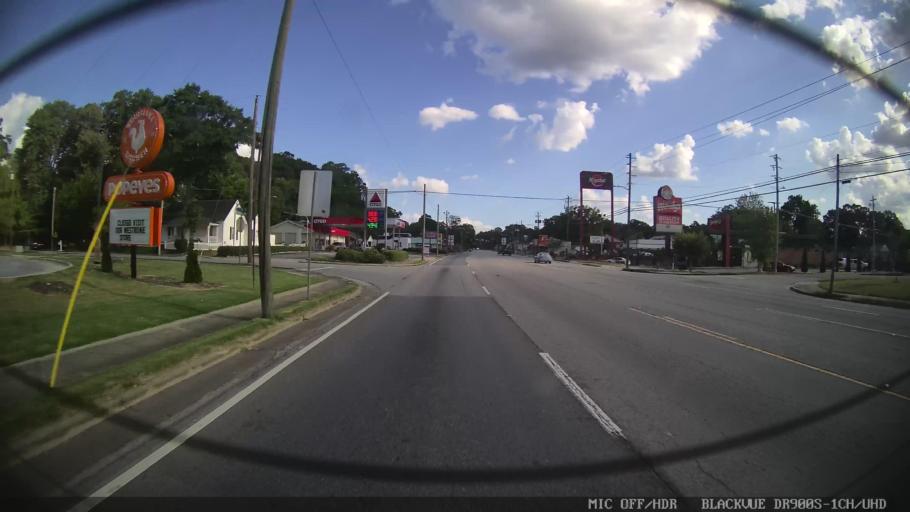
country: US
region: Georgia
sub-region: Floyd County
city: Rome
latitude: 34.2449
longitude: -85.1612
